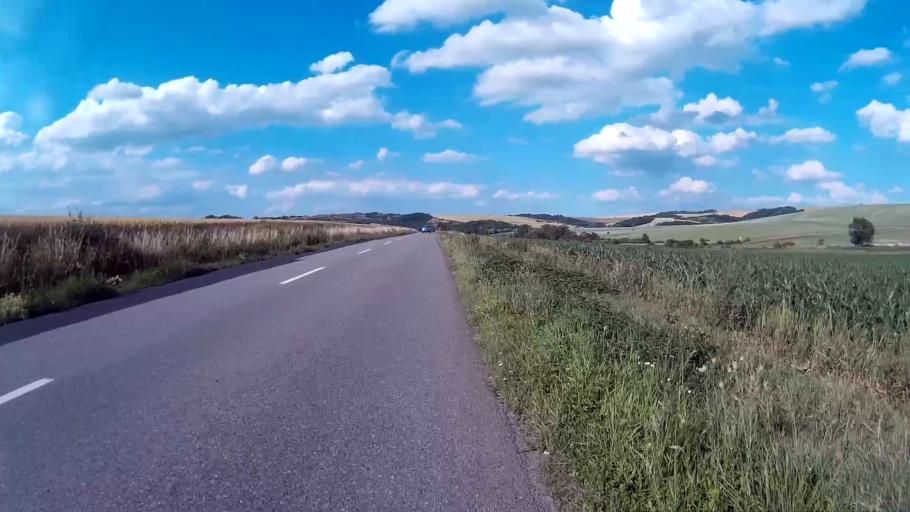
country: CZ
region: South Moravian
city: Tesany
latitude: 49.0323
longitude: 16.7881
